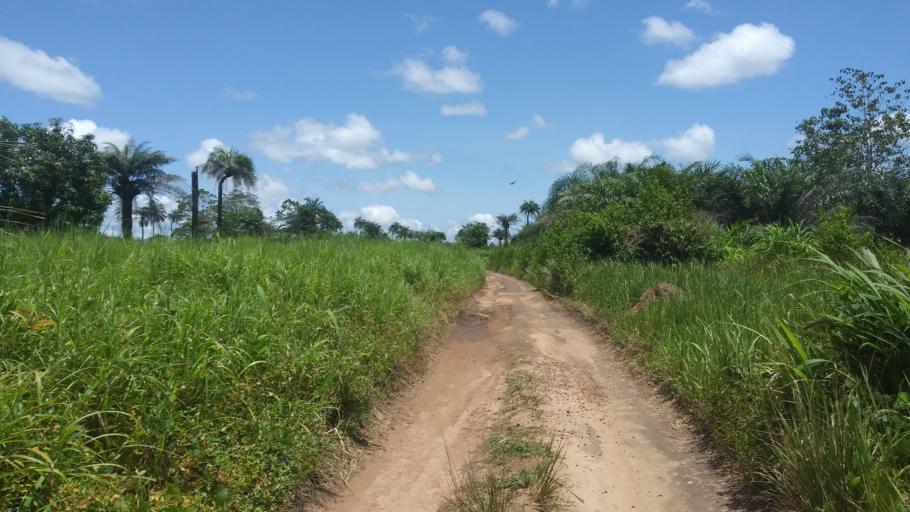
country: SL
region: Northern Province
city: Makeni
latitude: 8.8874
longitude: -12.0137
